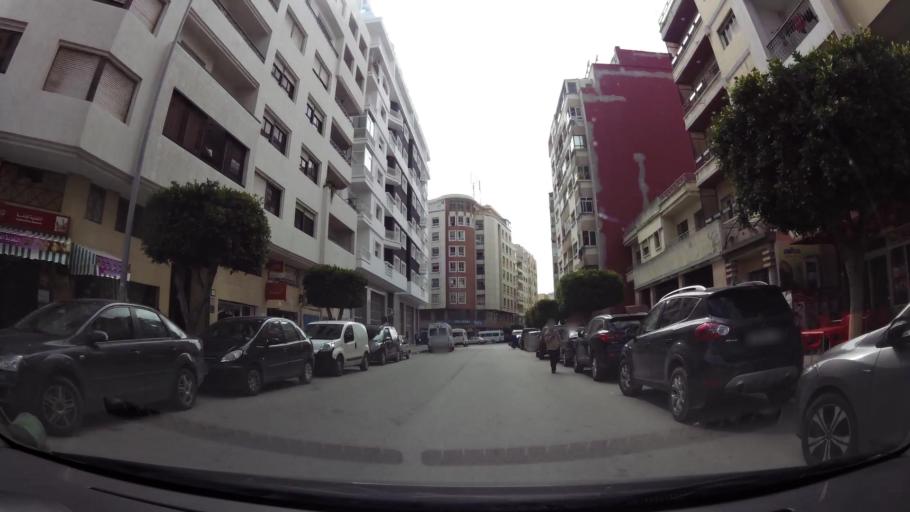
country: MA
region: Tanger-Tetouan
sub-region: Tanger-Assilah
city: Tangier
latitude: 35.7694
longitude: -5.8135
